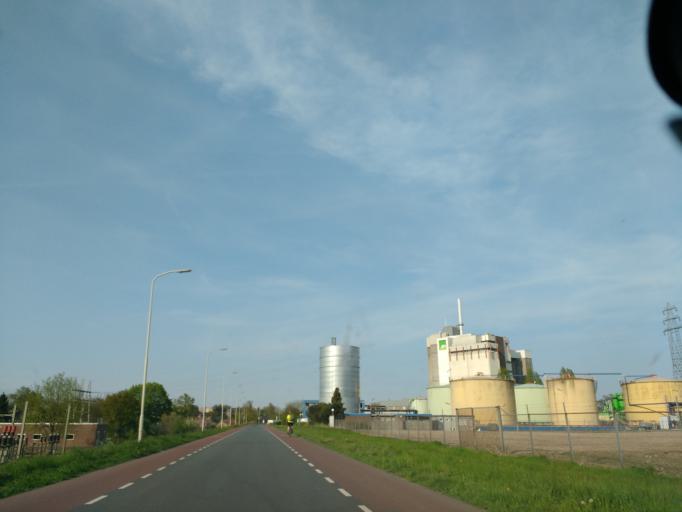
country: NL
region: Gelderland
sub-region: Gemeente Wageningen
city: Wageningen
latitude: 51.9592
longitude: 5.6504
